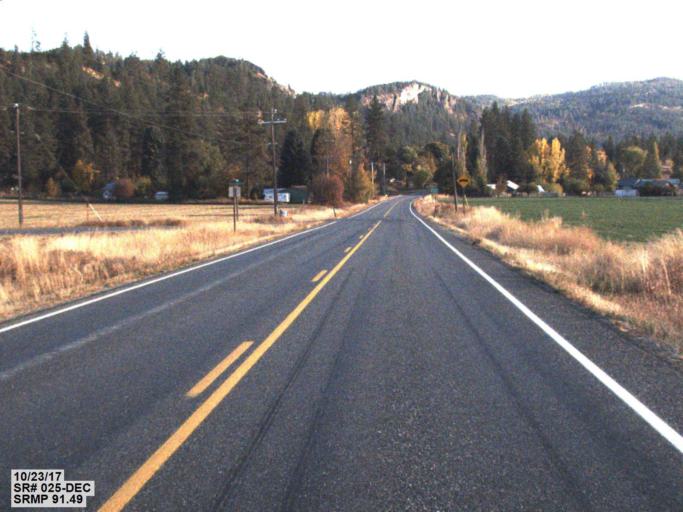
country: US
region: Washington
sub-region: Stevens County
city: Kettle Falls
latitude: 48.7175
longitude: -118.0272
